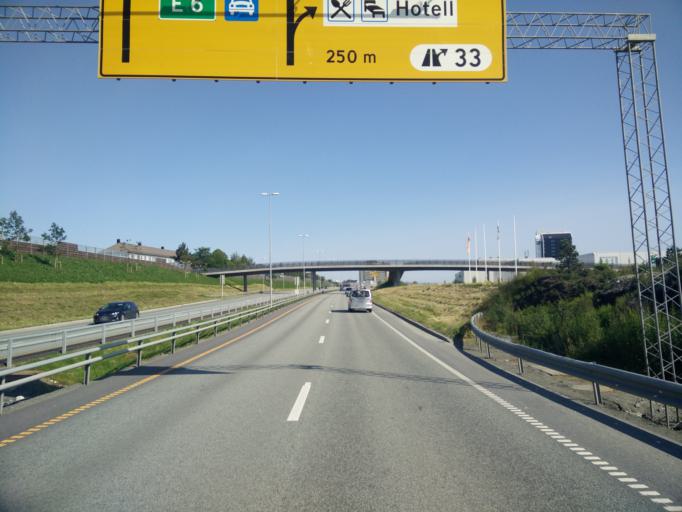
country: NO
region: Sor-Trondelag
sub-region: Trondheim
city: Trondheim
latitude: 63.3551
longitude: 10.3710
